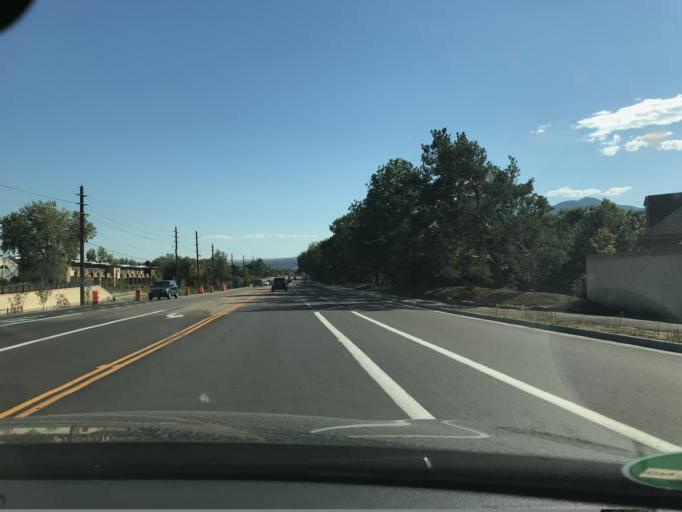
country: US
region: Colorado
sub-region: Boulder County
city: Boulder
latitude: 40.0433
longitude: -105.2586
